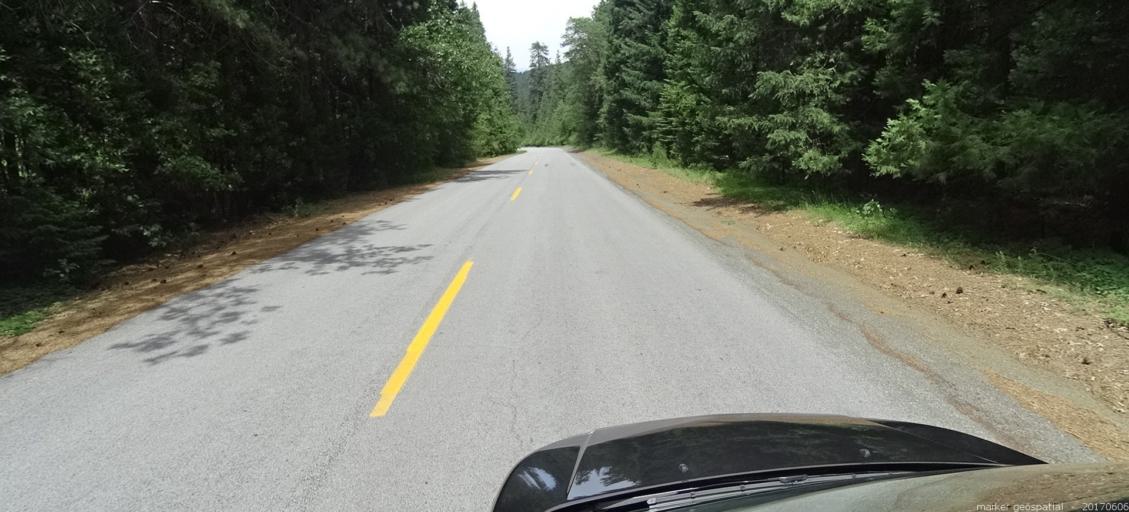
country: US
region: California
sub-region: Siskiyou County
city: Dunsmuir
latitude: 41.2447
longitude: -122.2608
